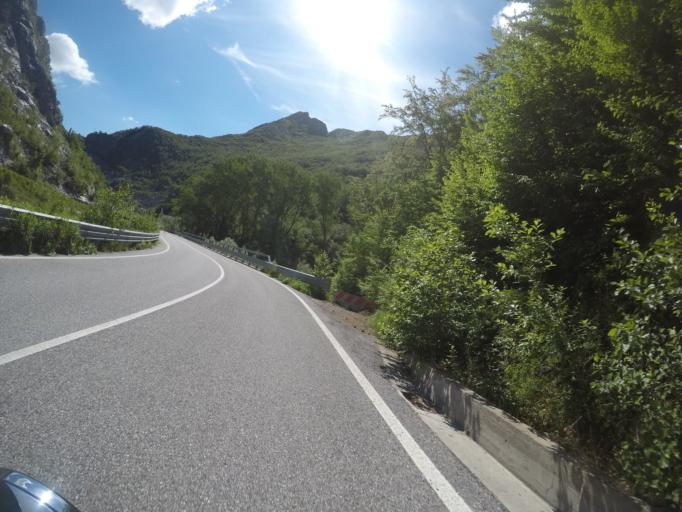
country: IT
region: Tuscany
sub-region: Provincia di Lucca
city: Fontana delle Monache
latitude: 44.0568
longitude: 10.2664
